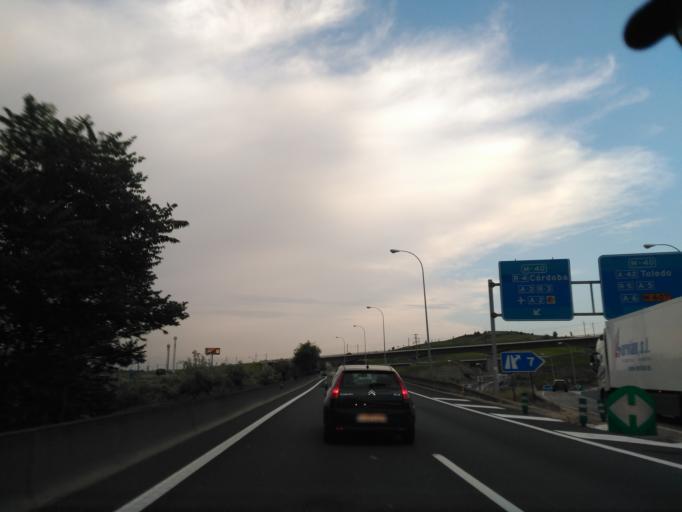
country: ES
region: Madrid
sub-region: Provincia de Madrid
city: Villaverde
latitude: 40.3588
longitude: -3.6786
